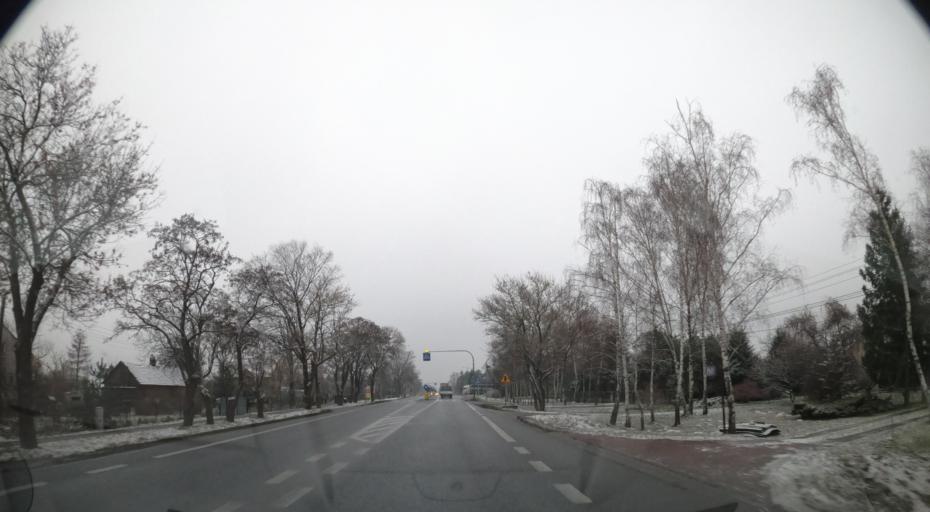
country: PL
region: Masovian Voivodeship
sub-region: Powiat warszawski zachodni
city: Blonie
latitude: 52.1997
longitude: 20.5899
